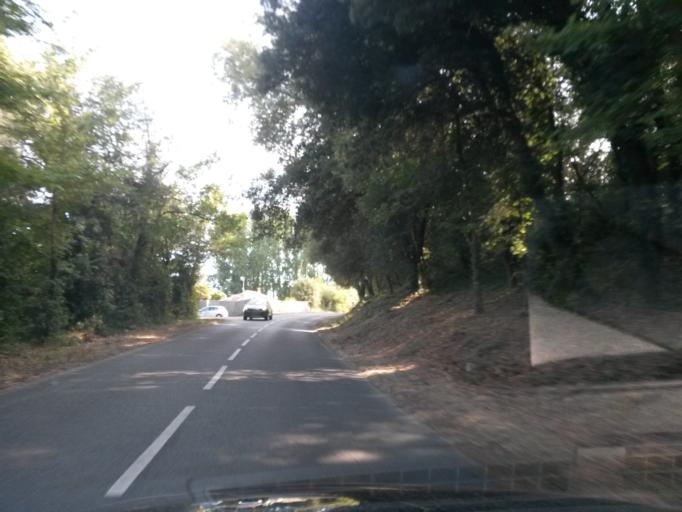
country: FR
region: Pays de la Loire
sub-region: Departement de la Vendee
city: Olonne-sur-Mer
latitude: 46.5368
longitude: -1.8129
